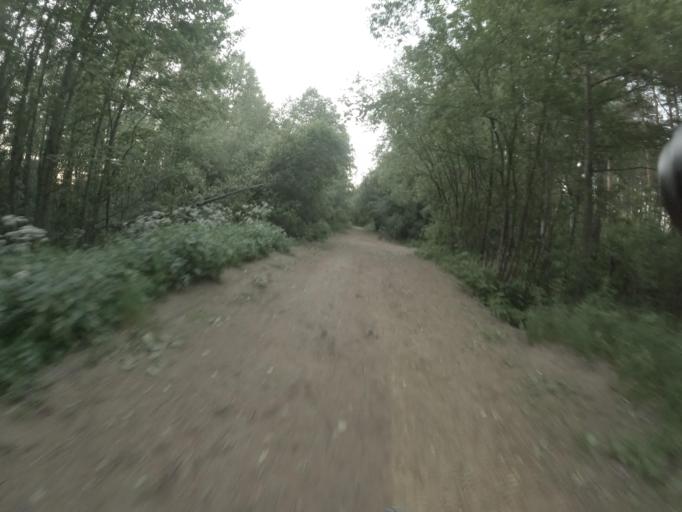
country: RU
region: St.-Petersburg
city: Krasnogvargeisky
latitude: 59.9875
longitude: 30.5312
